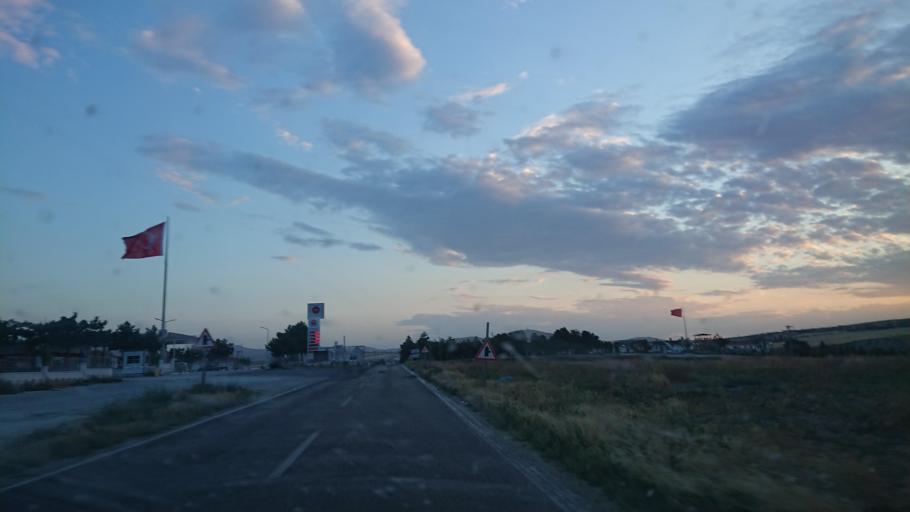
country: TR
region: Aksaray
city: Balci
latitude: 38.7653
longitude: 34.0928
